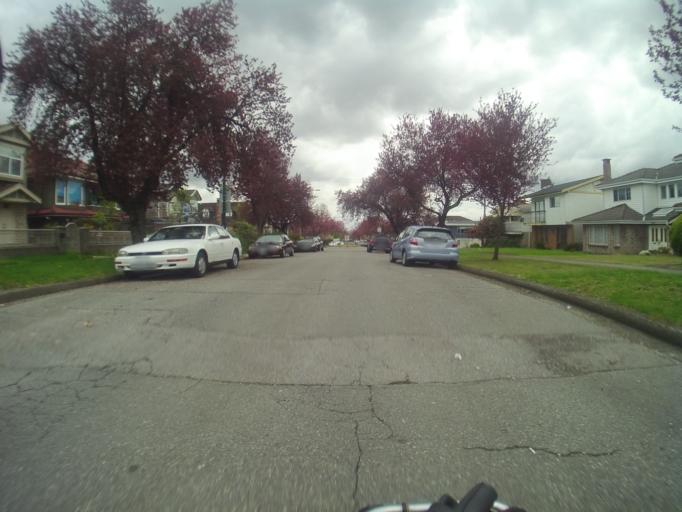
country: CA
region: British Columbia
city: Vancouver
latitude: 49.2223
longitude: -123.0747
